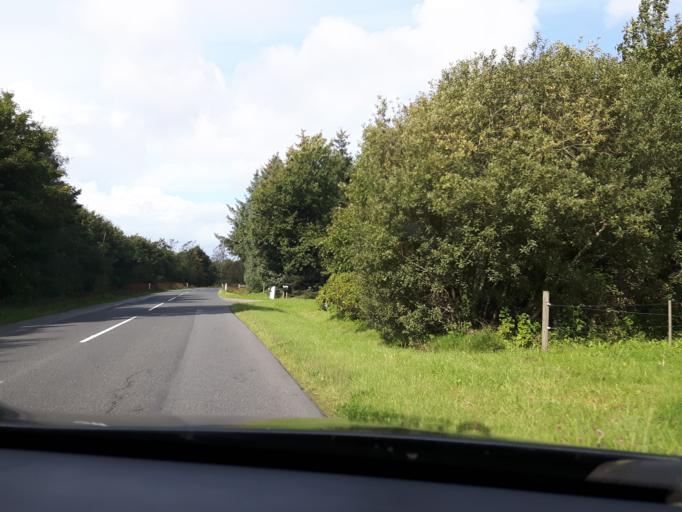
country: DK
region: North Denmark
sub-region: Jammerbugt Kommune
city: Kas
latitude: 57.1877
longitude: 9.5894
